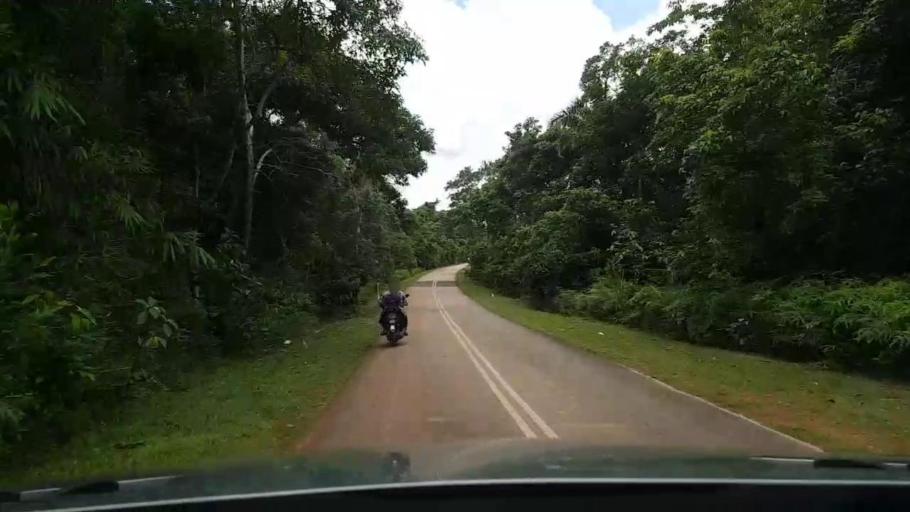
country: MY
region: Pahang
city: Pekan
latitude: 3.1309
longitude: 102.9749
